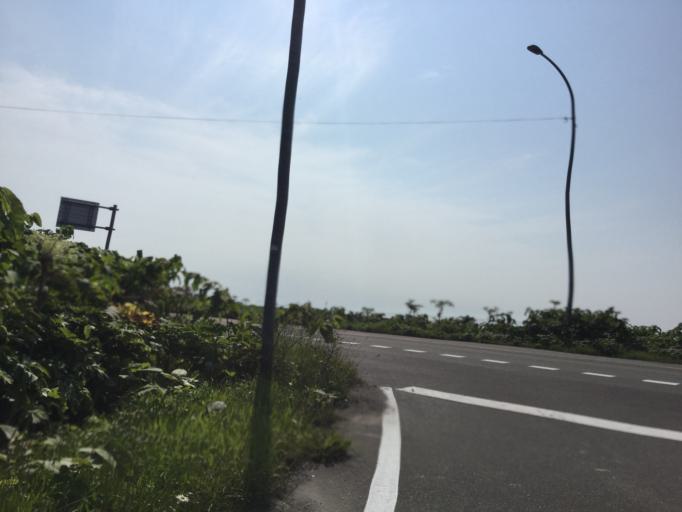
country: JP
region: Hokkaido
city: Makubetsu
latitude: 45.4975
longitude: 141.8871
